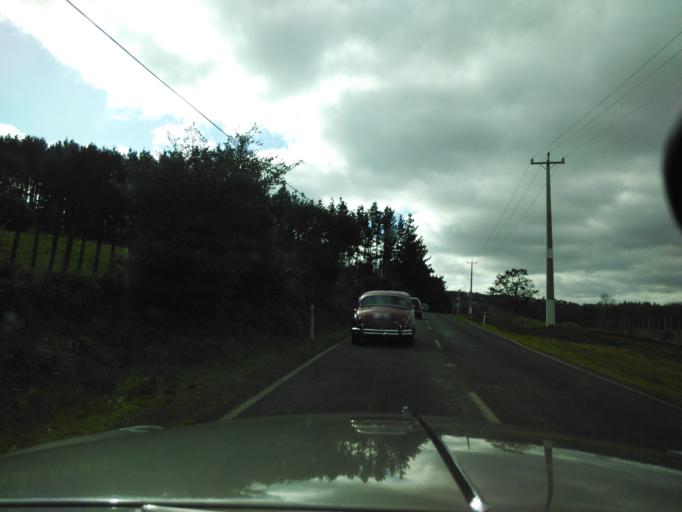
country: NZ
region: Auckland
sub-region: Auckland
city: Red Hill
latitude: -37.1396
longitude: 175.0387
